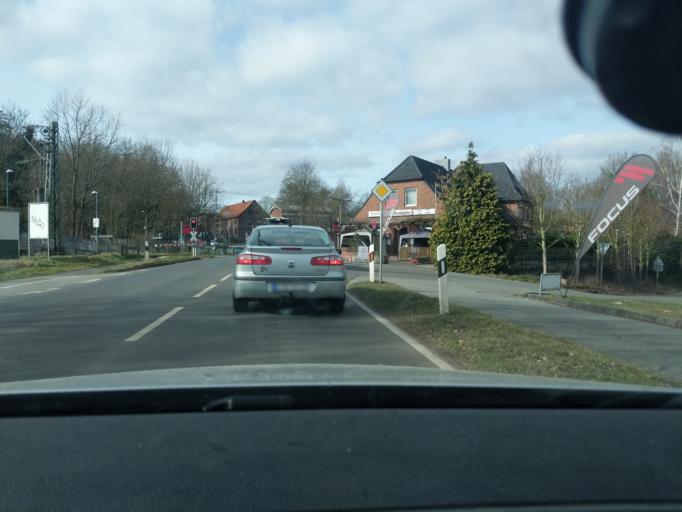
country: DE
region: Lower Saxony
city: Dollern
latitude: 53.5452
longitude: 9.5589
